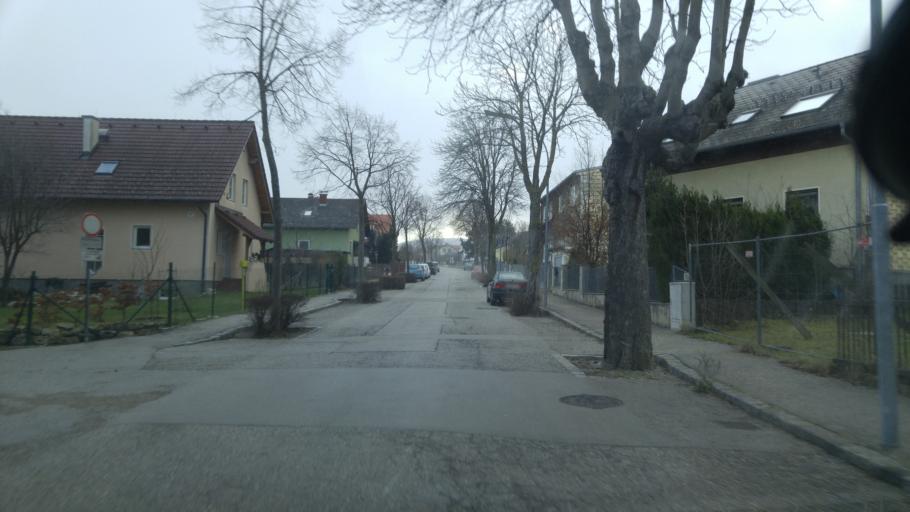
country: AT
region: Lower Austria
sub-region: Politischer Bezirk Baden
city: Baden
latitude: 47.9982
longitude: 16.2113
